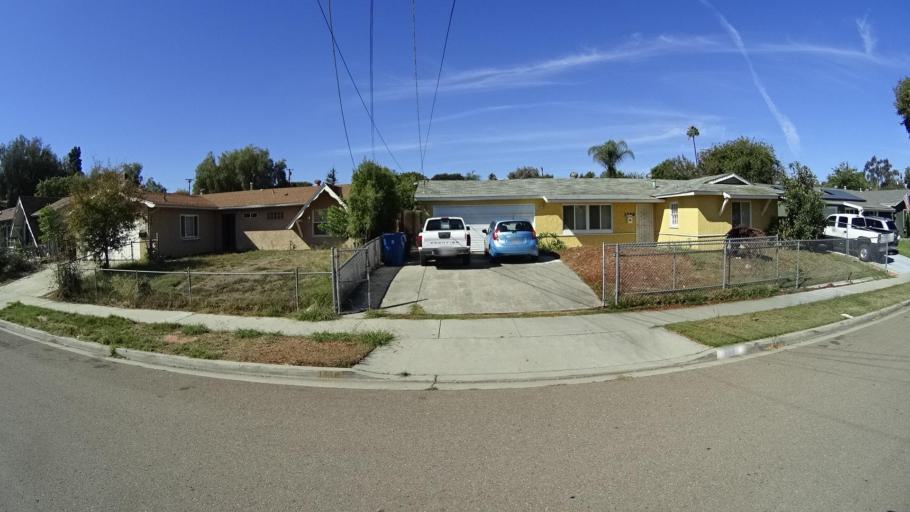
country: US
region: California
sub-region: San Diego County
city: Lemon Grove
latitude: 32.7226
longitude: -117.0193
